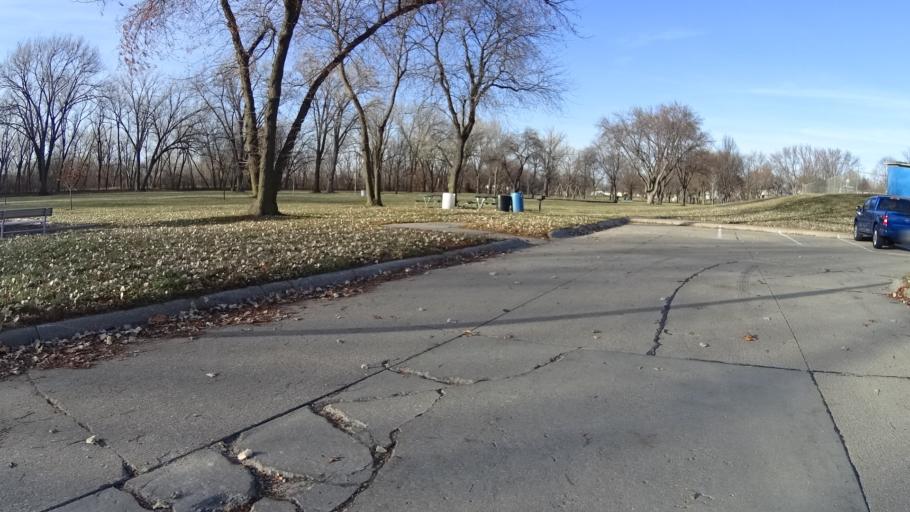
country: US
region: Nebraska
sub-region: Sarpy County
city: La Vista
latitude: 41.1850
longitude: -95.9994
